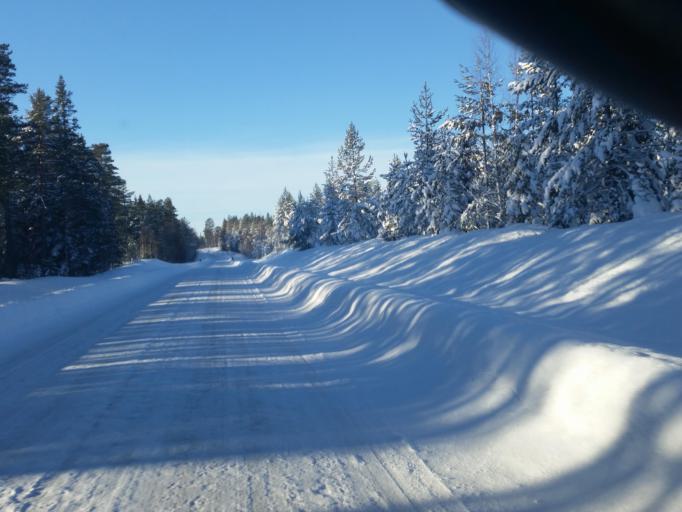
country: SE
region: Norrbotten
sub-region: Pitea Kommun
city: Roknas
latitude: 65.1958
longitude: 21.1061
